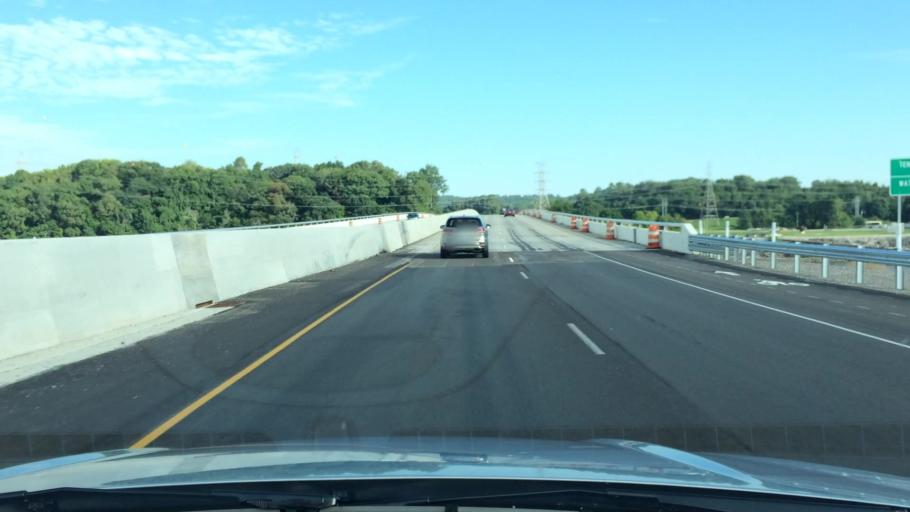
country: US
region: Tennessee
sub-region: Loudon County
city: Lenoir City
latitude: 35.7867
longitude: -84.2467
